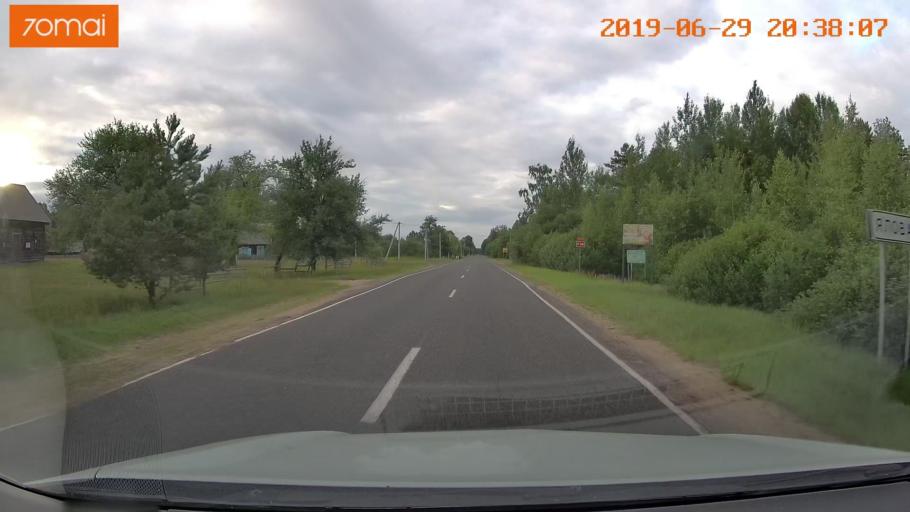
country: BY
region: Brest
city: Hantsavichy
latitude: 52.5463
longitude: 26.3652
